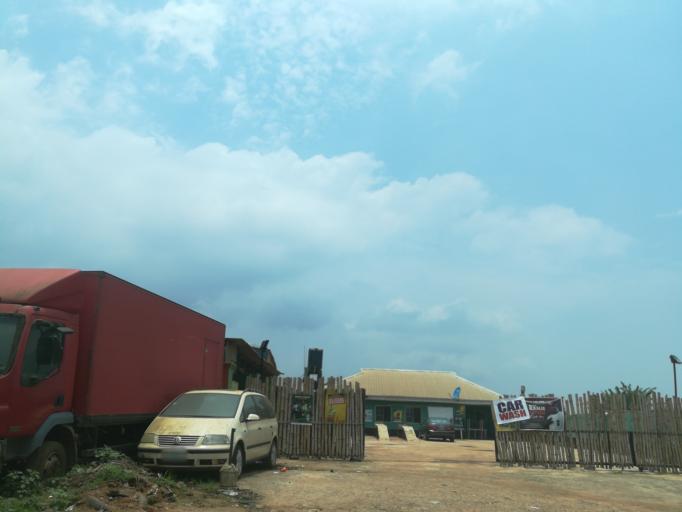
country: NG
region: Lagos
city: Ikorodu
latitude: 6.6263
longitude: 3.5479
